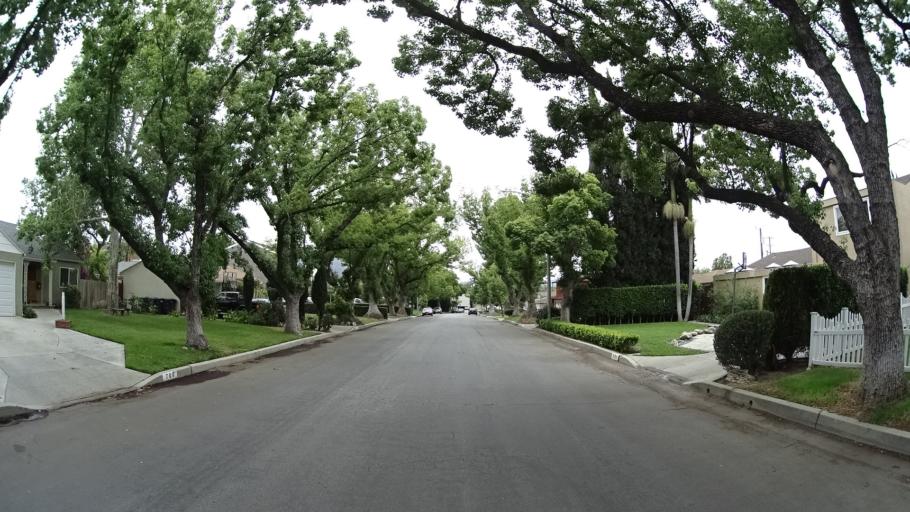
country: US
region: California
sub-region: Los Angeles County
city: Universal City
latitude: 34.1607
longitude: -118.3519
